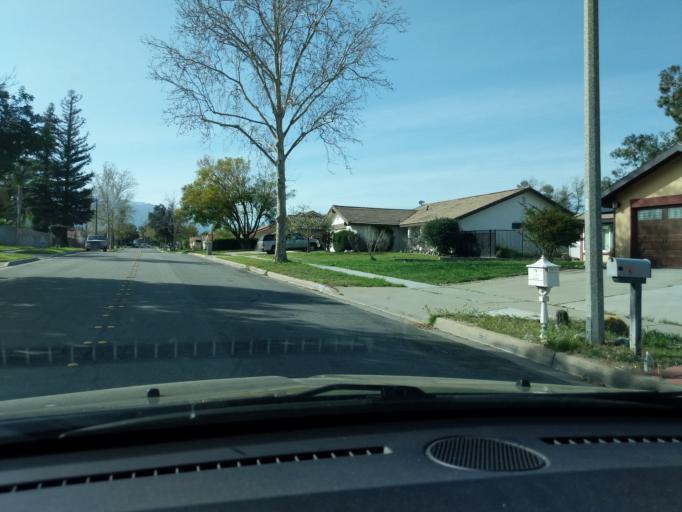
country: US
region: California
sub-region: San Bernardino County
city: Muscoy
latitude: 34.1405
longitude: -117.3681
